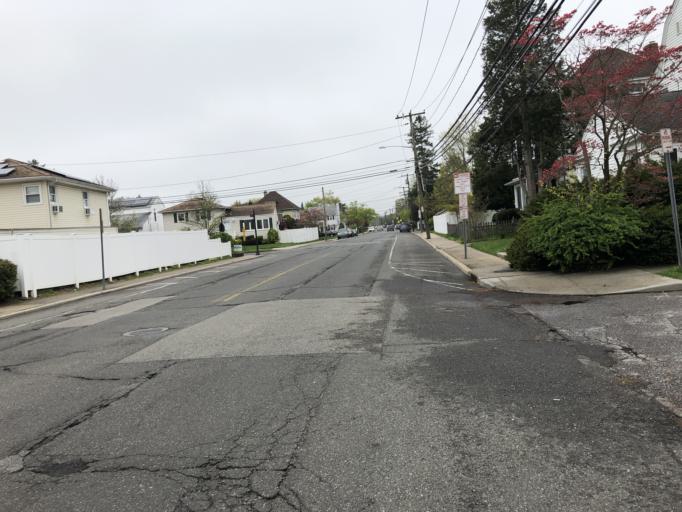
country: US
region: New York
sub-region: Nassau County
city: Lynbrook
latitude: 40.6478
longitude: -73.6778
